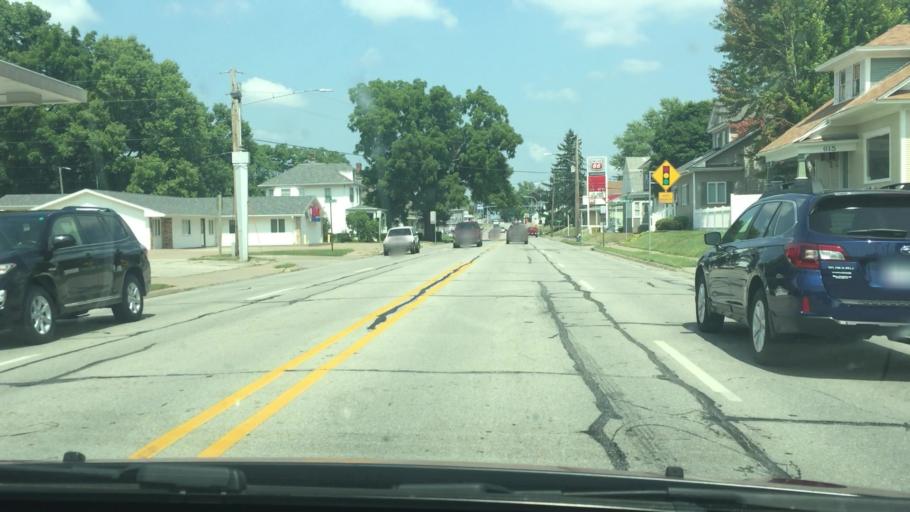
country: US
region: Iowa
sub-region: Muscatine County
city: Muscatine
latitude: 41.4322
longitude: -91.0310
